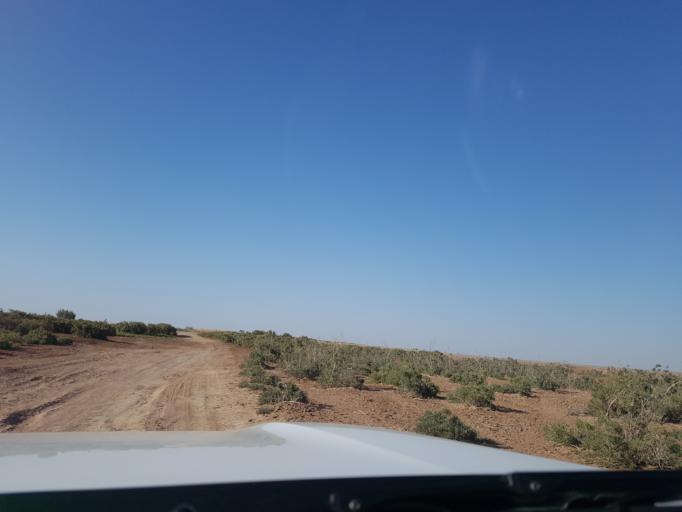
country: IR
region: Razavi Khorasan
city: Sarakhs
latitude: 36.9945
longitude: 61.3884
